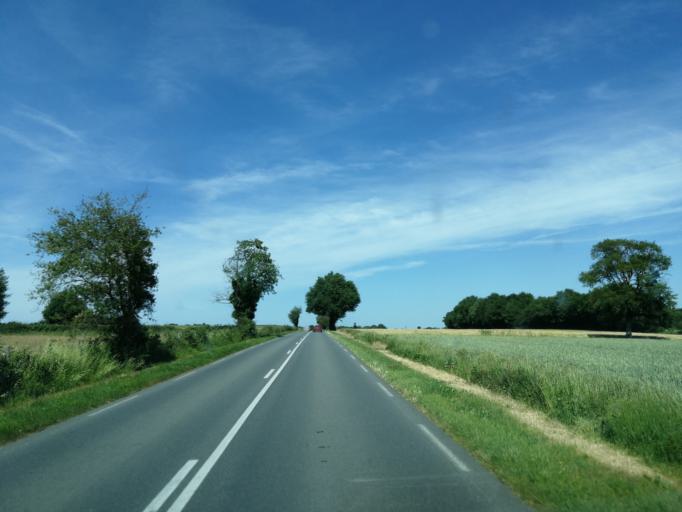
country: FR
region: Poitou-Charentes
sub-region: Departement des Deux-Sevres
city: Saint-Varent
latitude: 46.9214
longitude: -0.2636
